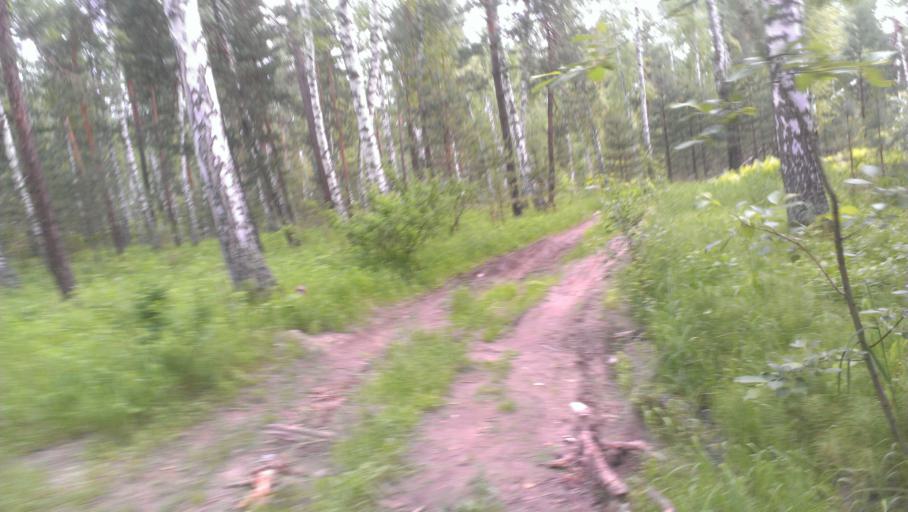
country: RU
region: Altai Krai
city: Sannikovo
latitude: 53.3469
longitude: 84.0408
